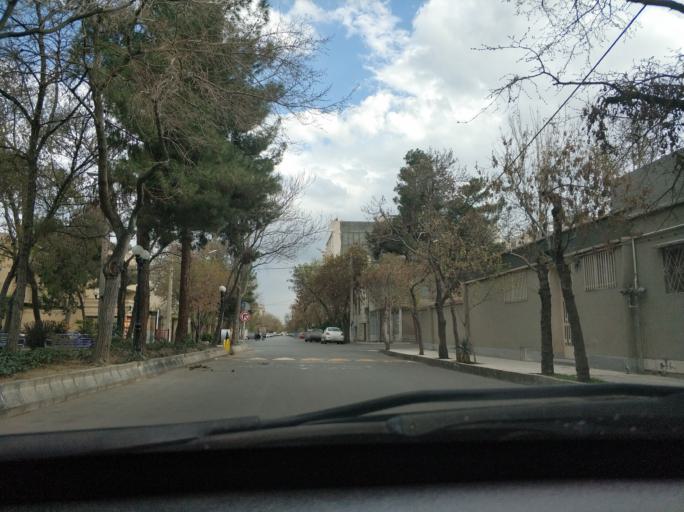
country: IR
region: Razavi Khorasan
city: Mashhad
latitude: 36.2754
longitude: 59.5954
